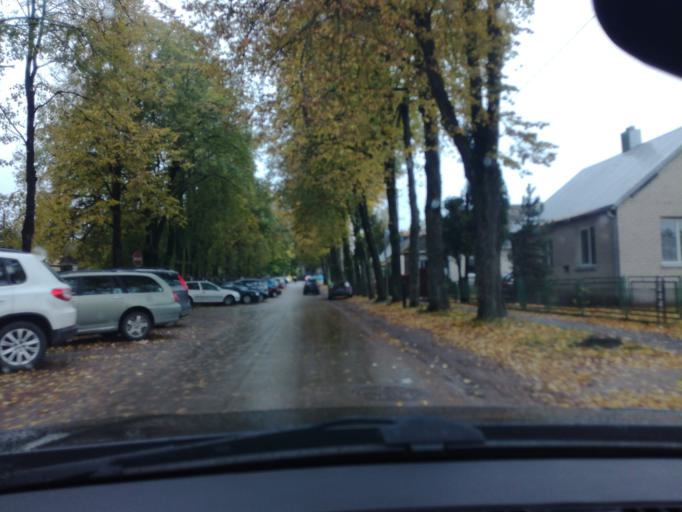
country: LT
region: Alytaus apskritis
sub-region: Alytus
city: Alytus
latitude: 54.4004
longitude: 24.0399
